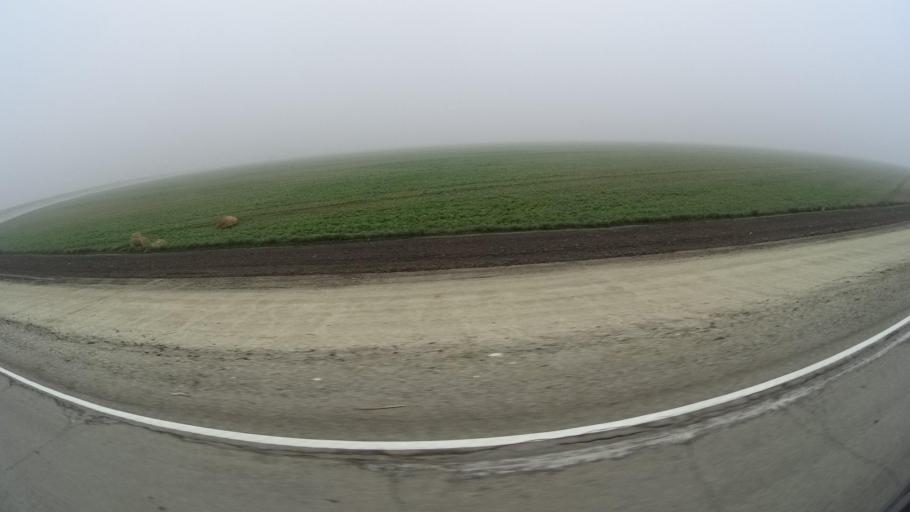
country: US
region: California
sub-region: Kern County
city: Buttonwillow
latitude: 35.4352
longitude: -119.5436
